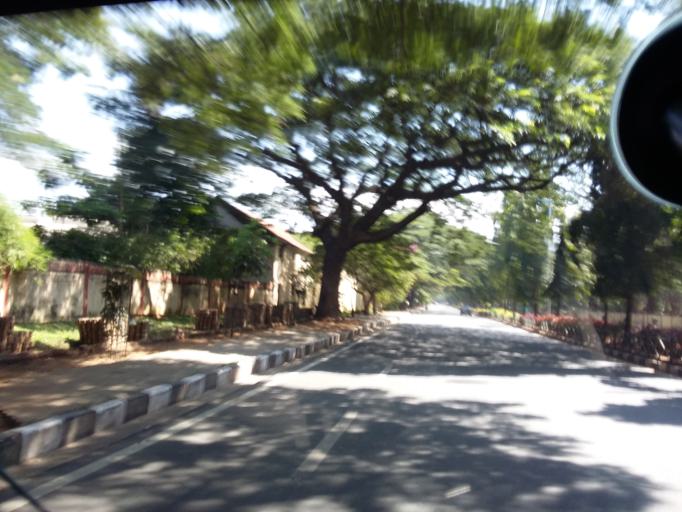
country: IN
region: Karnataka
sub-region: Bangalore Urban
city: Bangalore
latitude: 12.9769
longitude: 77.6099
